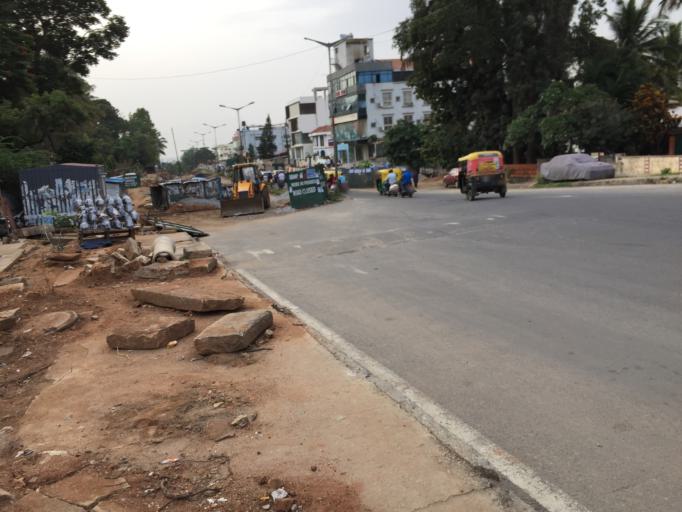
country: IN
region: Karnataka
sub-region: Bangalore Urban
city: Bangalore
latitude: 12.9291
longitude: 77.5449
